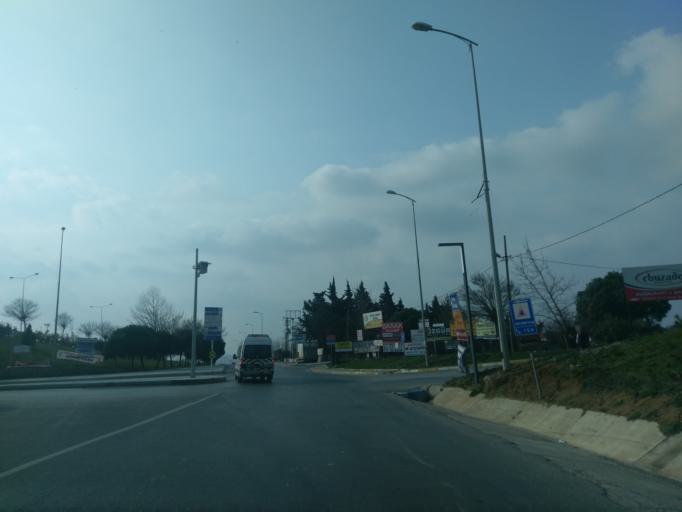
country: TR
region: Istanbul
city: Silivri
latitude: 41.0735
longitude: 28.2668
